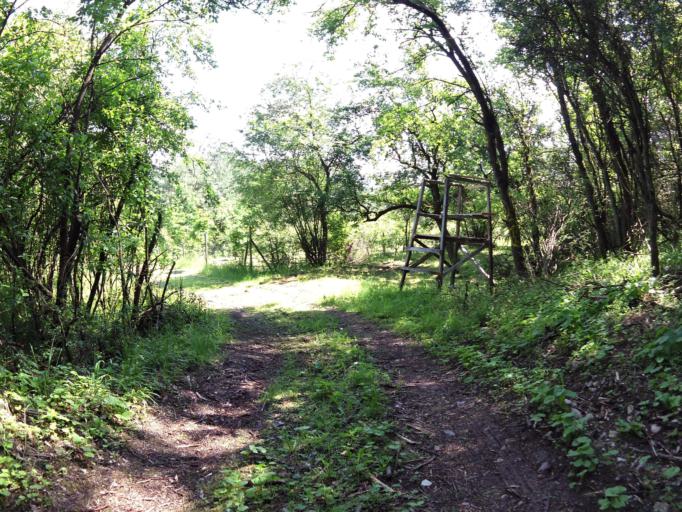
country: DE
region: Bavaria
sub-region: Regierungsbezirk Unterfranken
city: Eibelstadt
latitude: 49.7292
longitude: 10.0151
